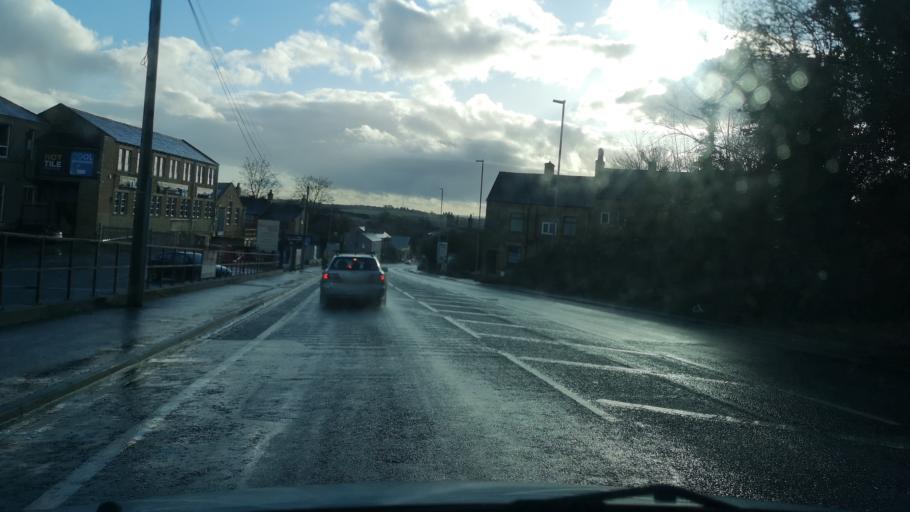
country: GB
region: England
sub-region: City and Borough of Leeds
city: Drighlington
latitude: 53.7348
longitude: -1.6570
